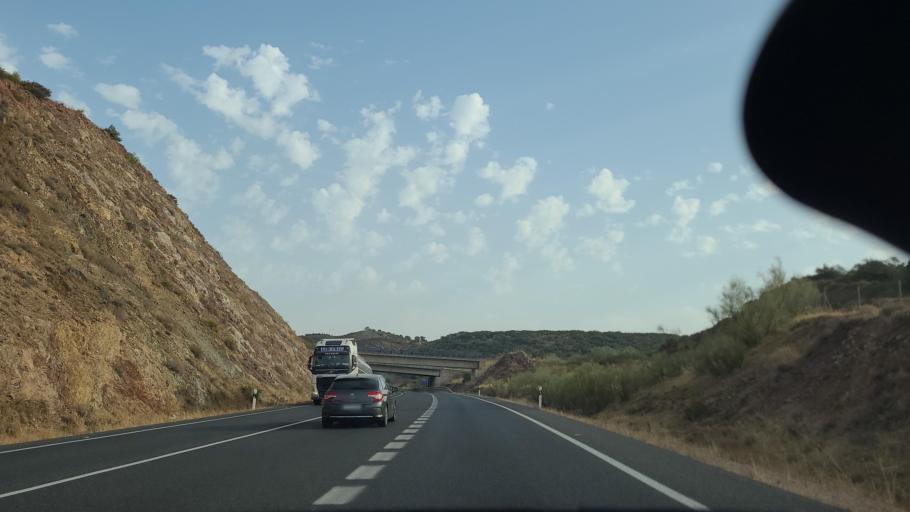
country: ES
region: Andalusia
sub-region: Province of Cordoba
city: Cordoba
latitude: 37.9391
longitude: -4.7625
